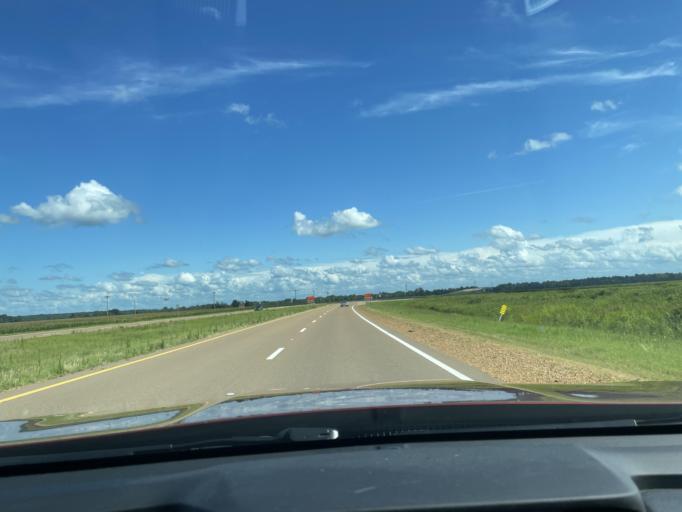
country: US
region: Mississippi
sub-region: Yazoo County
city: Yazoo City
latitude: 32.9445
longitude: -90.4159
